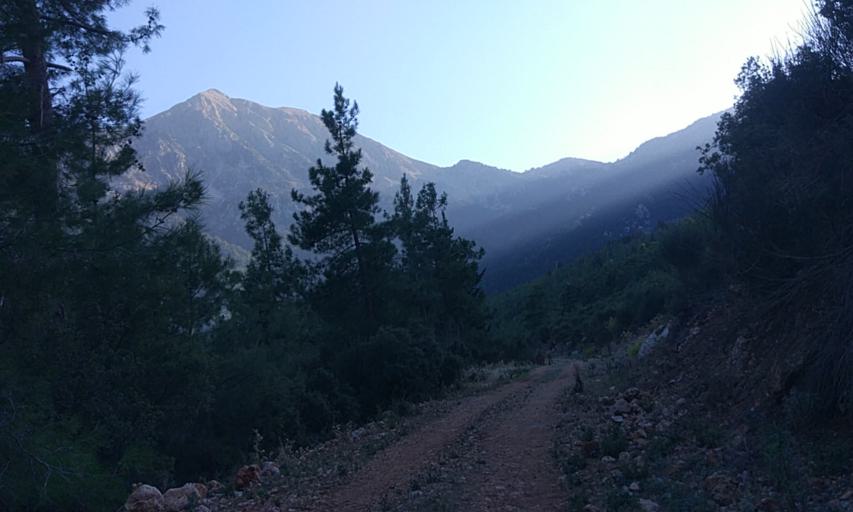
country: TR
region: Antalya
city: Altinyaka
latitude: 36.5905
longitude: 30.4268
